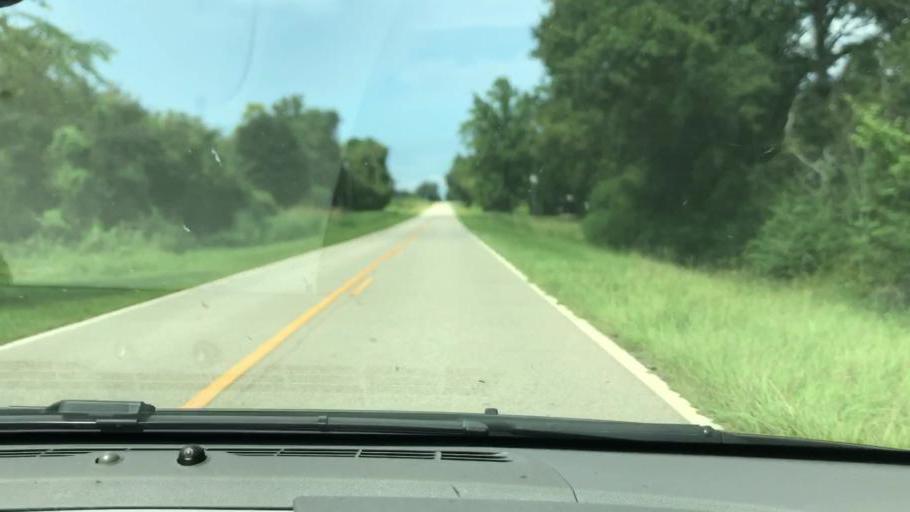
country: US
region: Georgia
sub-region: Seminole County
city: Donalsonville
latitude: 31.1271
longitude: -84.9954
